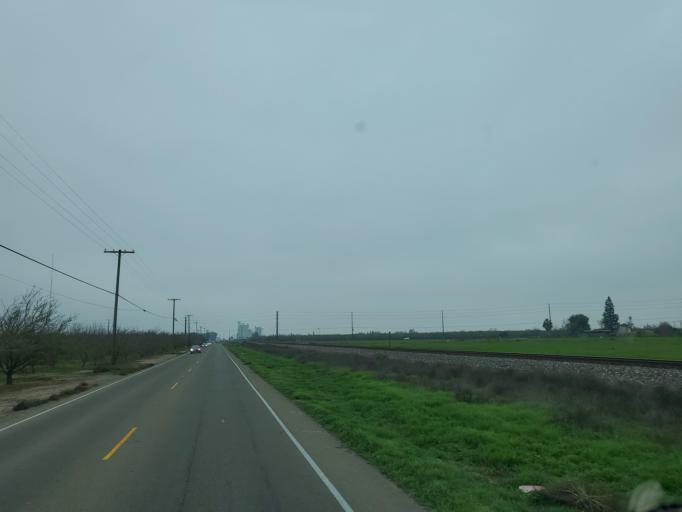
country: US
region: California
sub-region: Stanislaus County
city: Hughson
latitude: 37.5837
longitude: -120.8556
